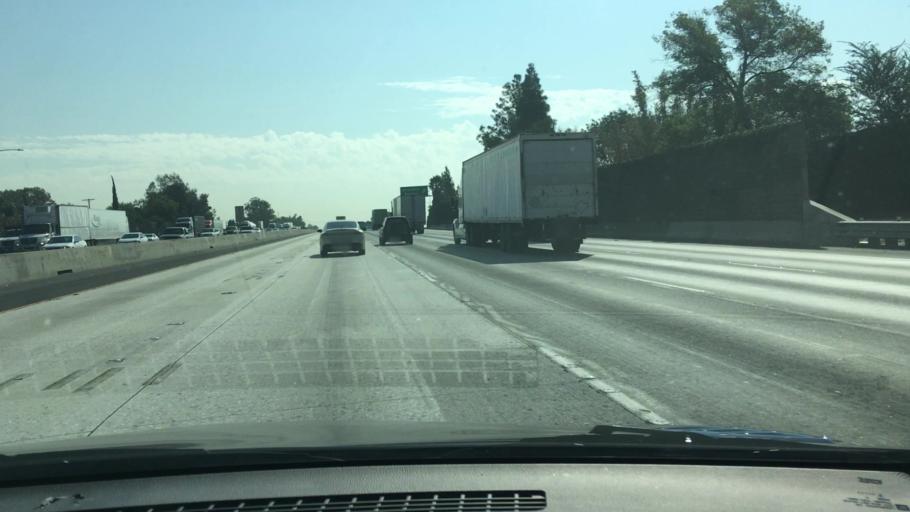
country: US
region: California
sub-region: San Bernardino County
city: Chino
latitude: 34.0303
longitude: -117.6743
